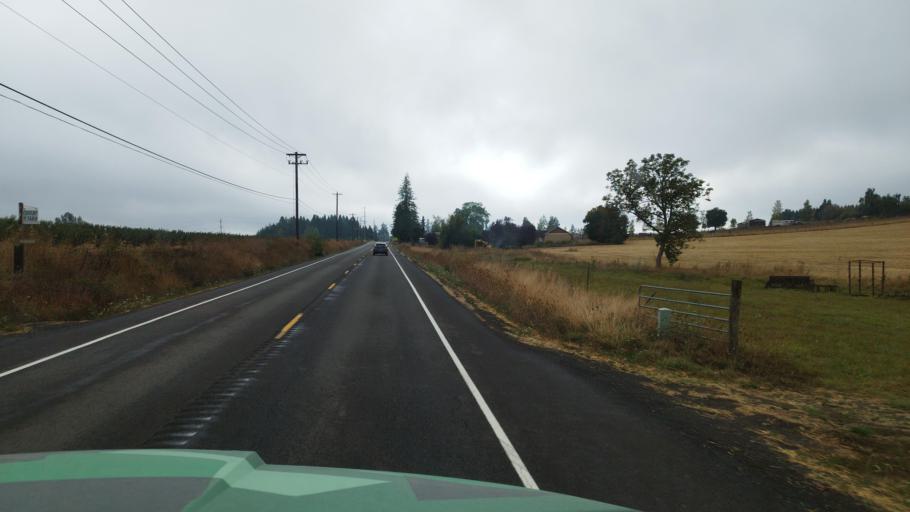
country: US
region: Oregon
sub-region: Yamhill County
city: Yamhill
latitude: 45.3244
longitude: -123.1794
